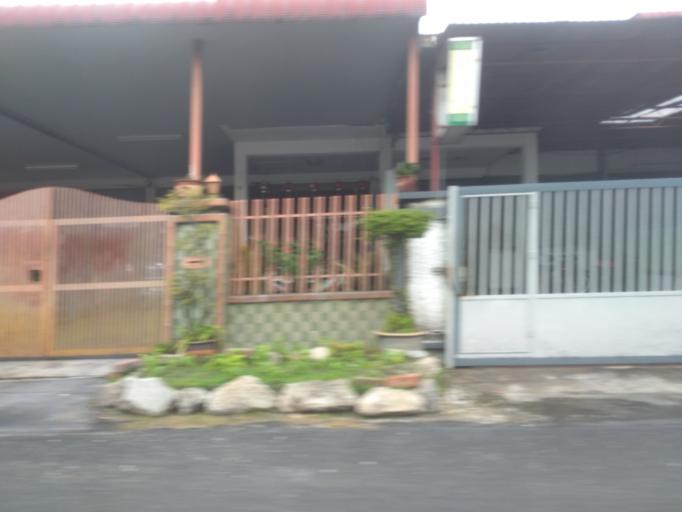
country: MY
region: Penang
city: Bukit Mertajam
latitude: 5.3613
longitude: 100.4500
